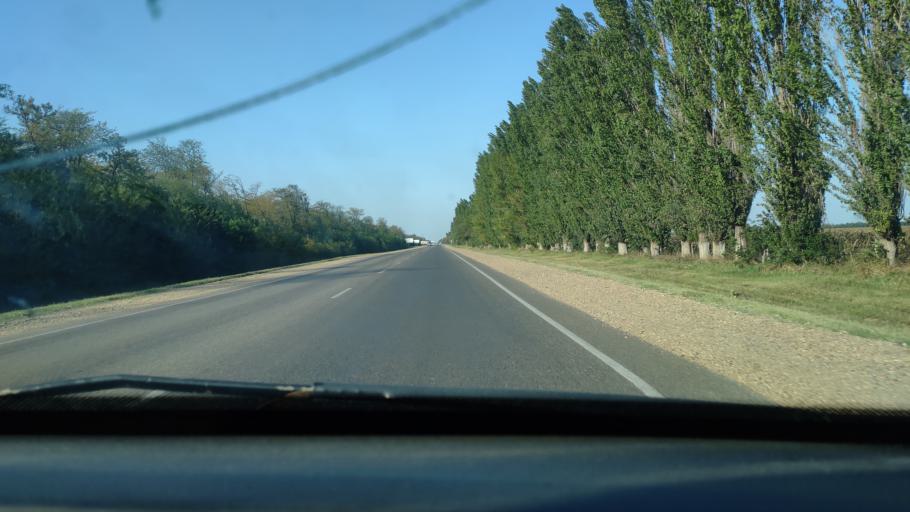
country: RU
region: Krasnodarskiy
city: Novotitarovskaya
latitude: 45.2688
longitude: 39.0034
